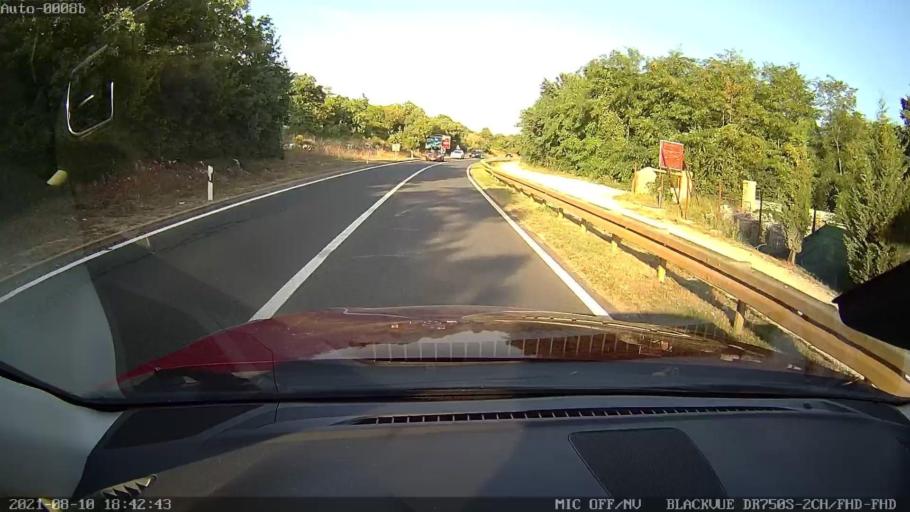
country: HR
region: Istarska
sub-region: Grad Rovinj
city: Rovinj
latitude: 45.1016
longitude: 13.6874
